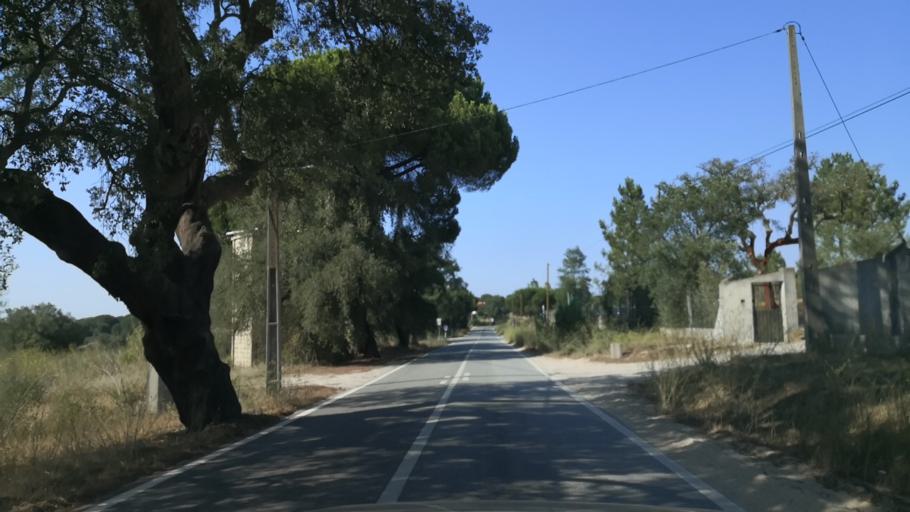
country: PT
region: Santarem
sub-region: Benavente
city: Poceirao
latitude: 38.7588
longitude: -8.6325
